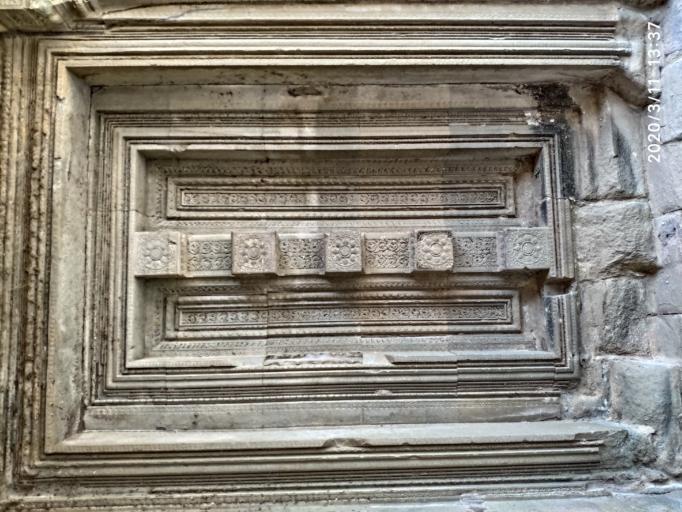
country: KH
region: Siem Reap
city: Siem Reap
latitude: 13.4116
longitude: 103.8618
